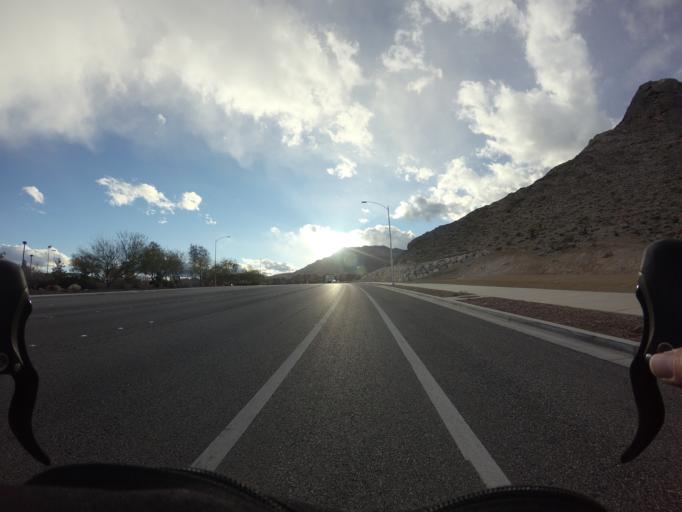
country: US
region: Nevada
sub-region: Clark County
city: Summerlin South
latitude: 36.2331
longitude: -115.3116
